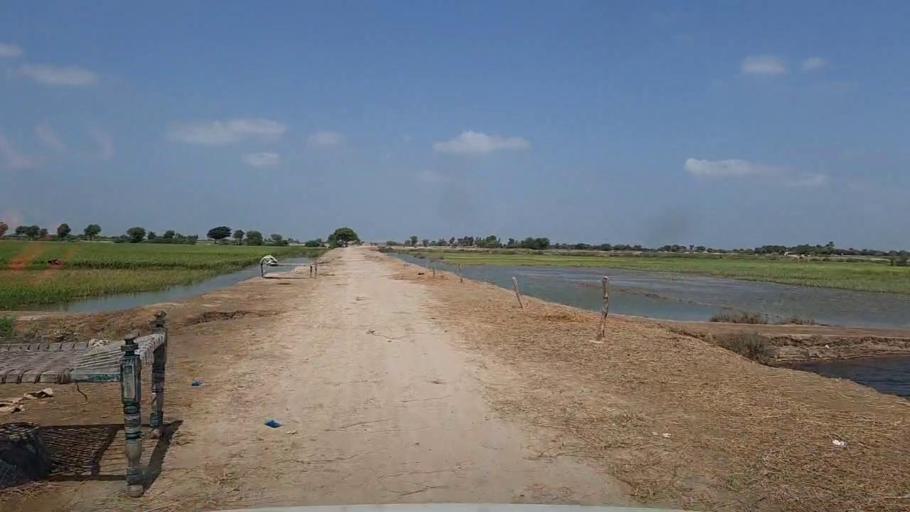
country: PK
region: Sindh
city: Kario
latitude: 24.6984
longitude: 68.5860
